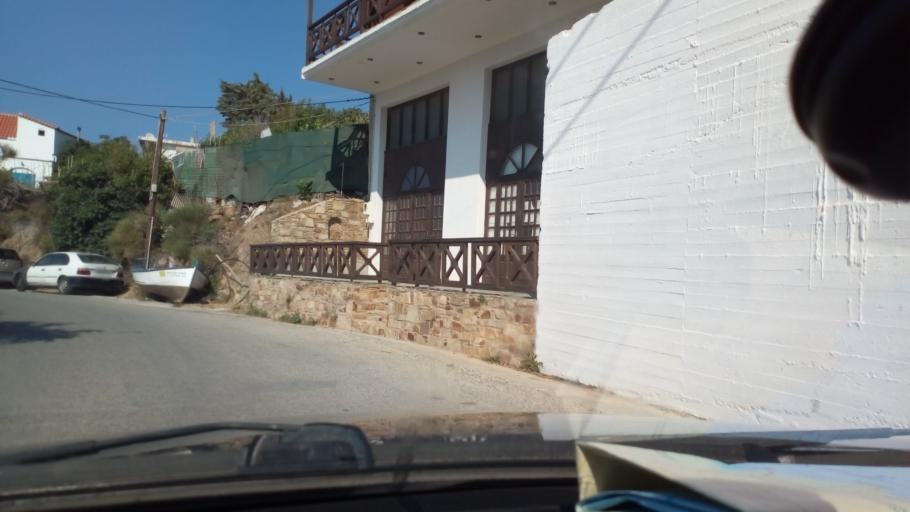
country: GR
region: North Aegean
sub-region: Nomos Samou
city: Agios Kirykos
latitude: 37.6343
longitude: 26.0859
